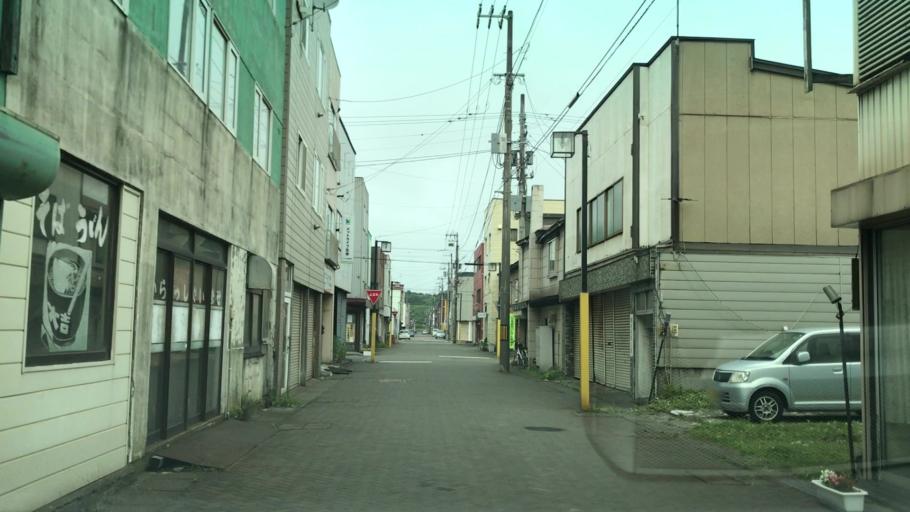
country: JP
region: Hokkaido
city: Muroran
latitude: 42.3341
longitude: 141.0100
